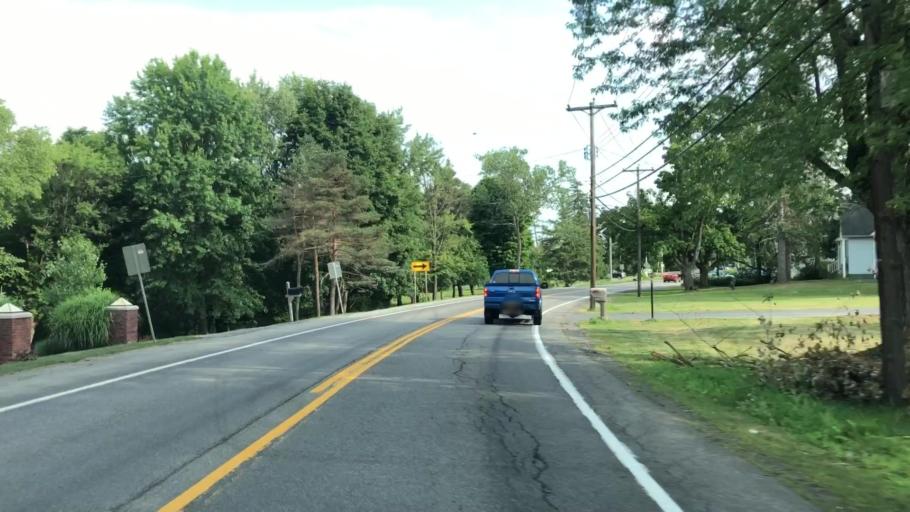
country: US
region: New York
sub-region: Erie County
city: Elma Center
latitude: 42.8408
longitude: -78.6372
